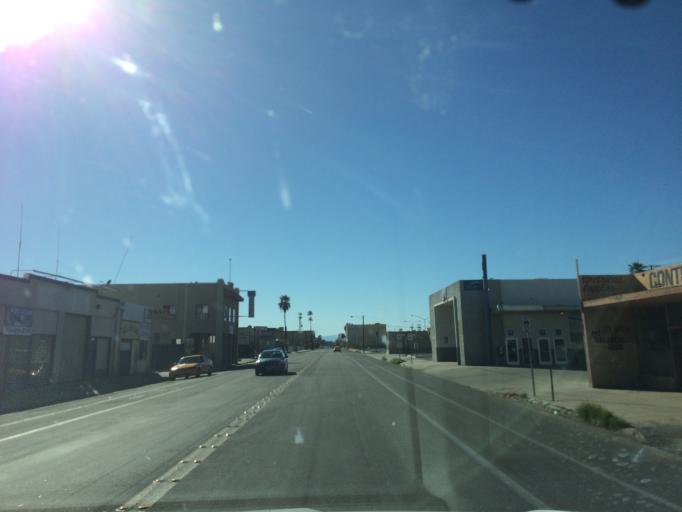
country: US
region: California
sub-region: Imperial County
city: El Centro
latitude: 32.7918
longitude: -115.5533
